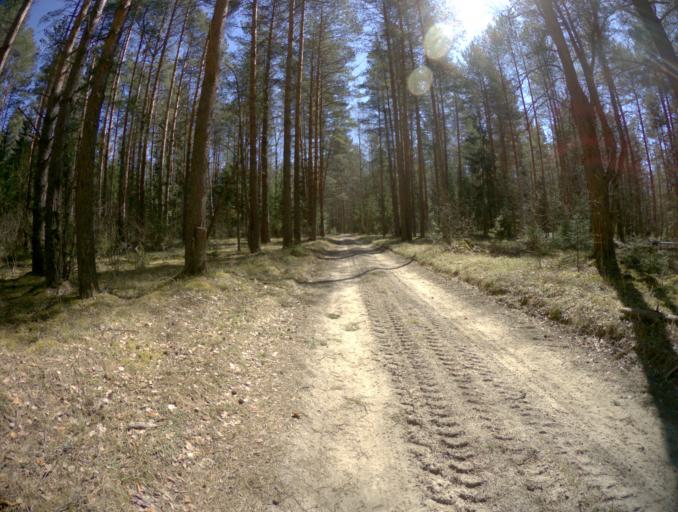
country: RU
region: Vladimir
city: Golovino
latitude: 55.9124
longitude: 40.4339
